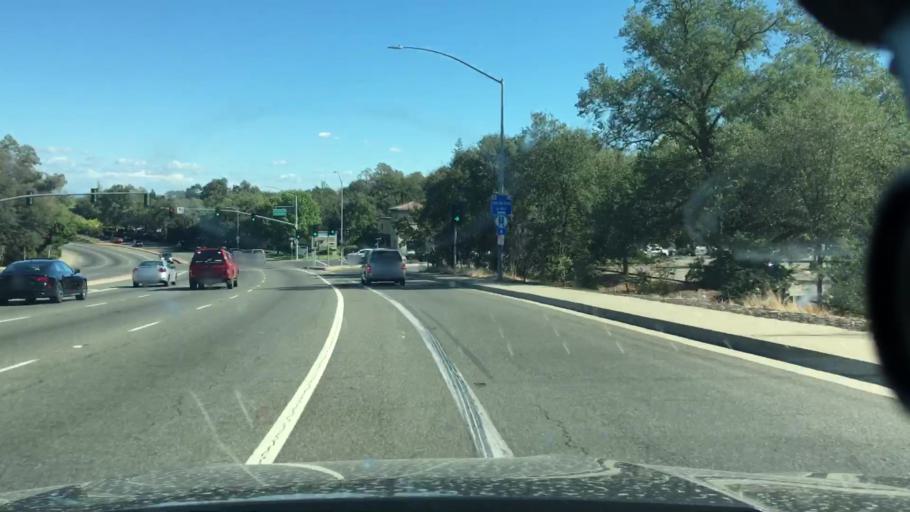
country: US
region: California
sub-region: Sacramento County
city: Foothill Farms
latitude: 38.6815
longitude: -121.3346
